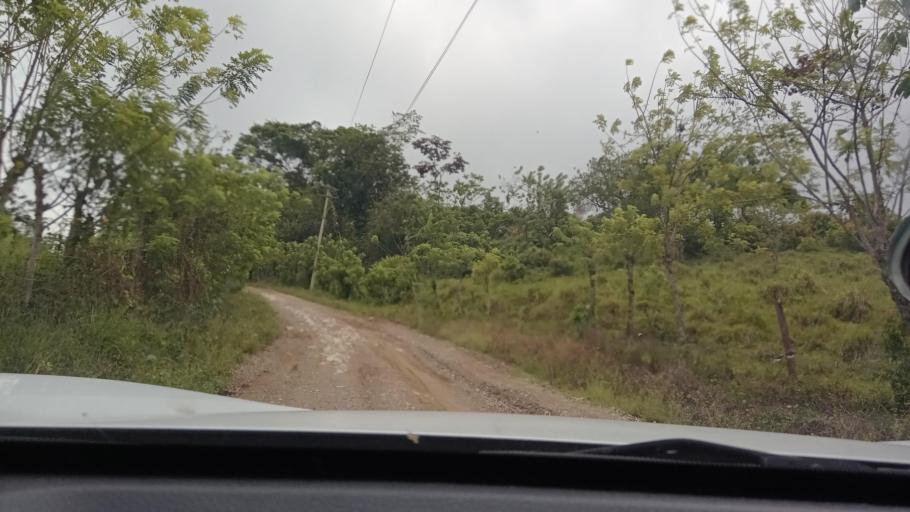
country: MX
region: Tabasco
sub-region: Huimanguillo
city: Francisco Rueda
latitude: 17.5185
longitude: -94.1228
